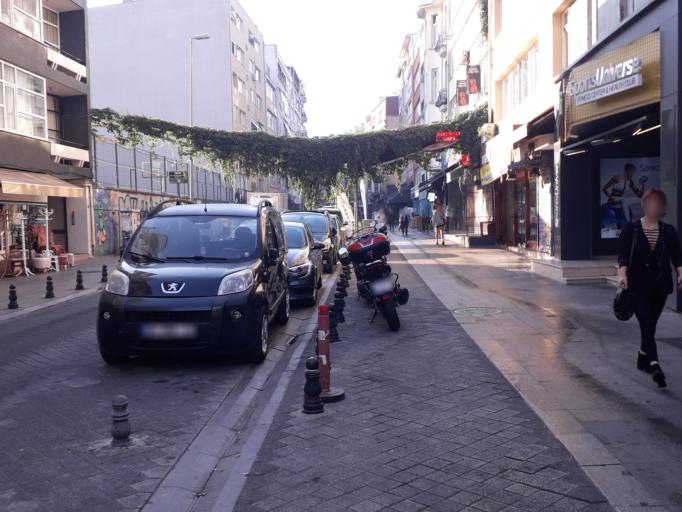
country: TR
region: Istanbul
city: UEskuedar
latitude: 40.9887
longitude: 29.0248
